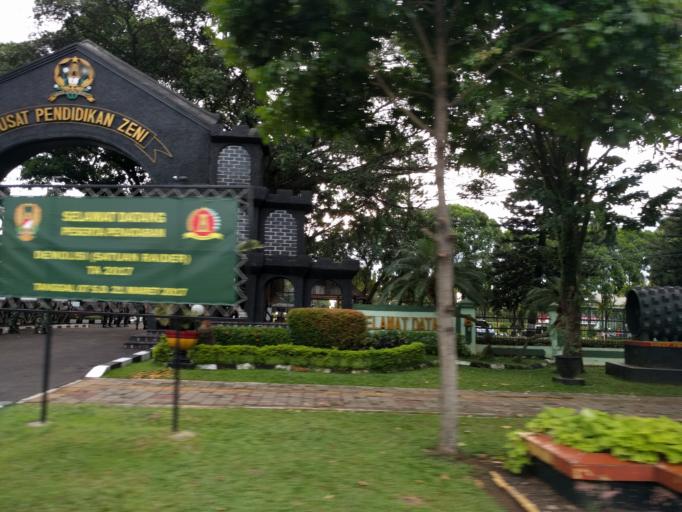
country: ID
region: West Java
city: Bogor
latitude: -6.5836
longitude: 106.7968
